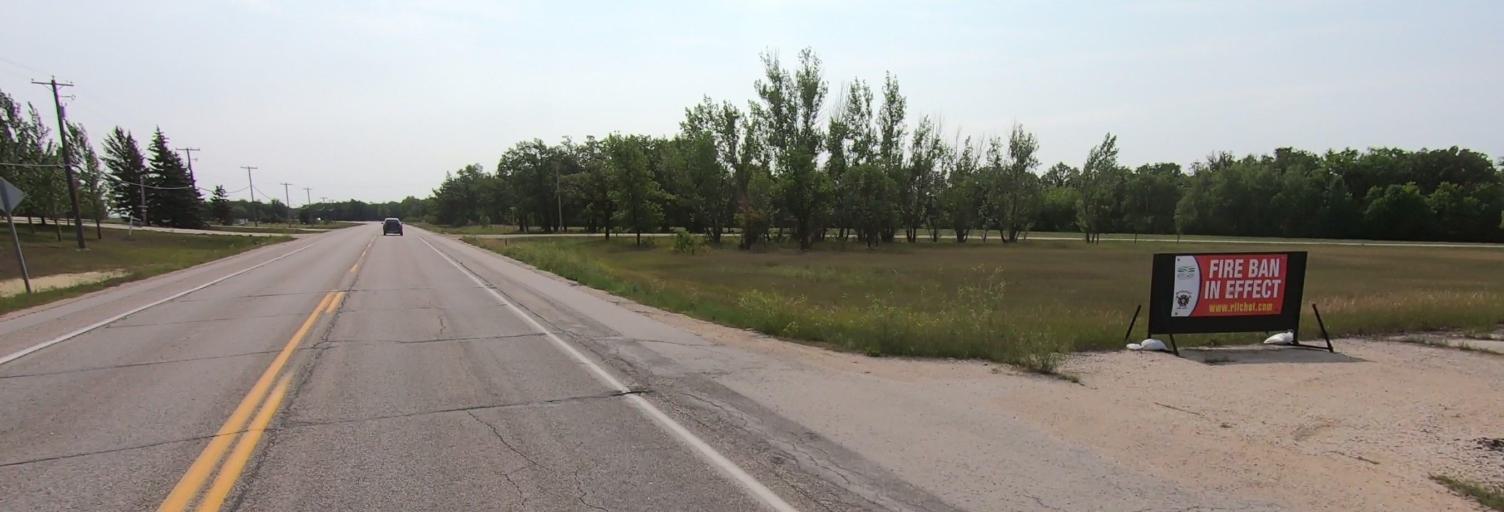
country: CA
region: Manitoba
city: Winnipeg
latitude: 49.7386
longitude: -97.1183
